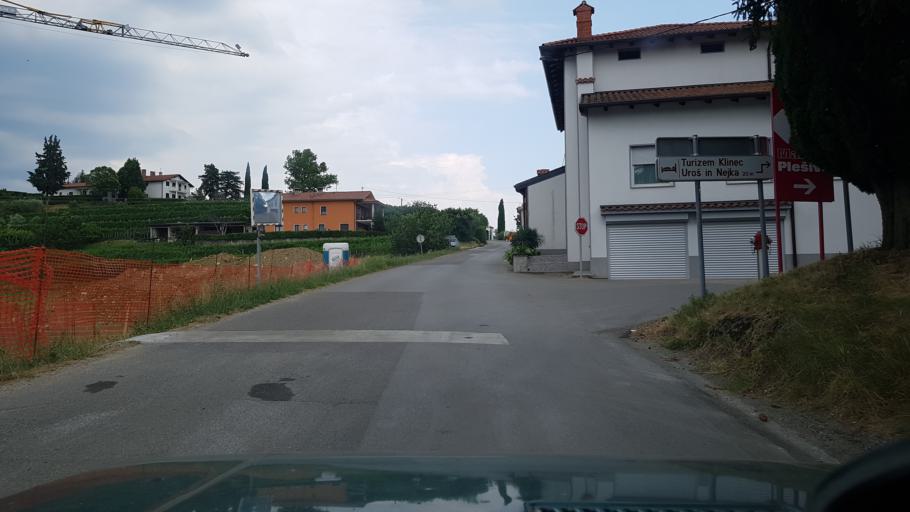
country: SI
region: Brda
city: Dobrovo
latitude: 45.9819
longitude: 13.5168
